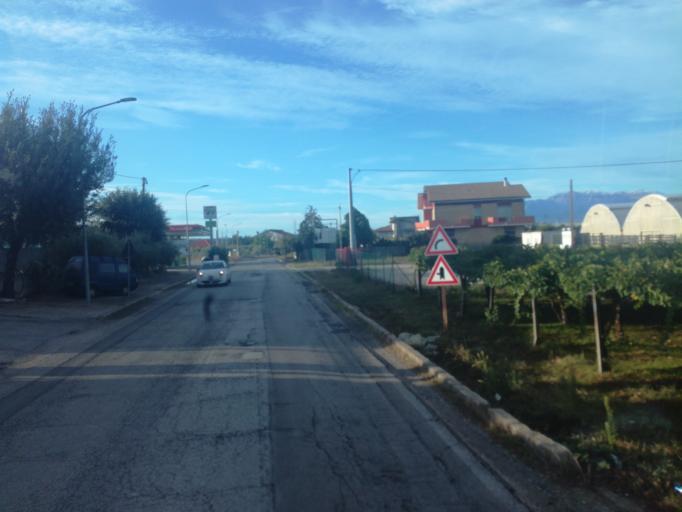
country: IT
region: Abruzzo
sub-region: Provincia di Chieti
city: Francavilla al Mare
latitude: 42.3923
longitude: 14.2964
